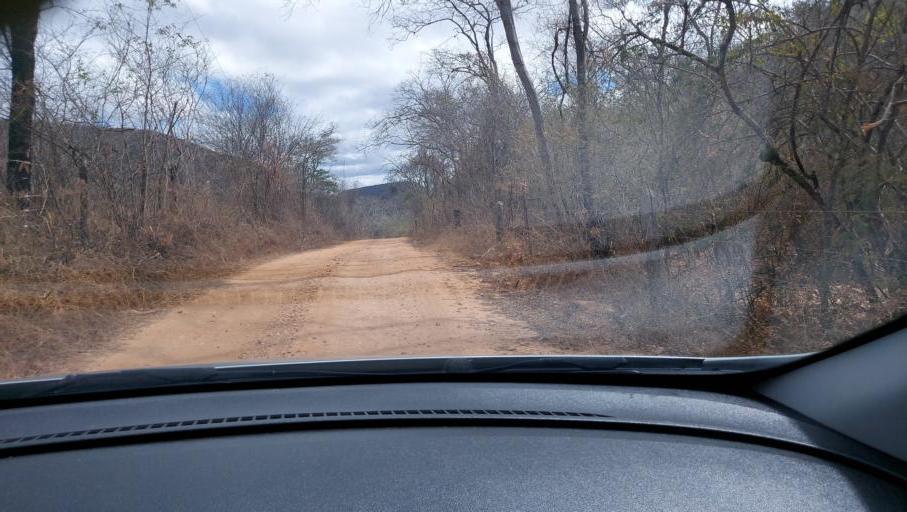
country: BR
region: Bahia
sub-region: Oliveira Dos Brejinhos
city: Beira Rio
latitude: -12.0814
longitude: -42.5435
